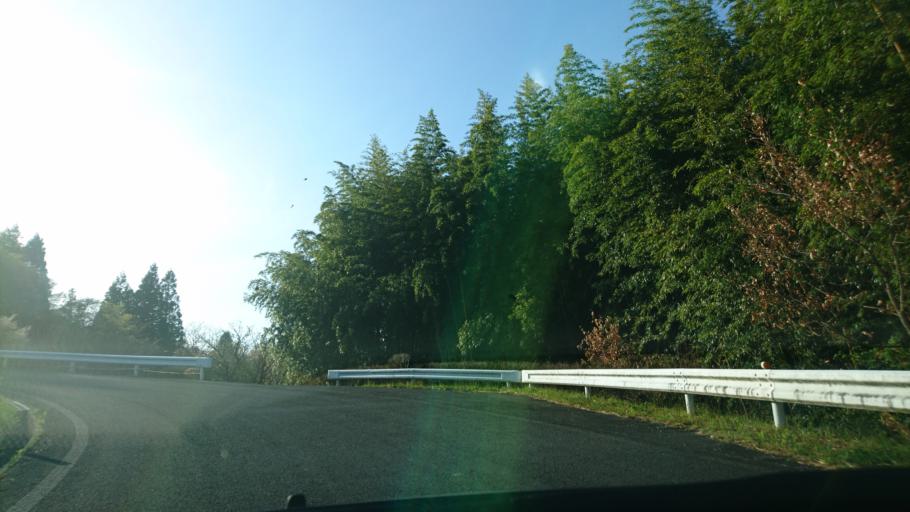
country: JP
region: Iwate
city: Ichinoseki
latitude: 38.8935
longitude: 141.2900
